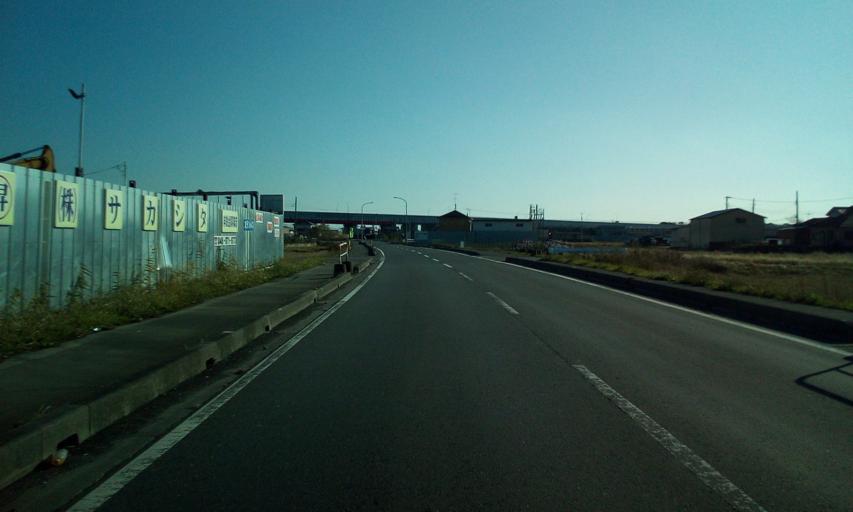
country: JP
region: Chiba
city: Nagareyama
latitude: 35.8774
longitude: 139.8881
